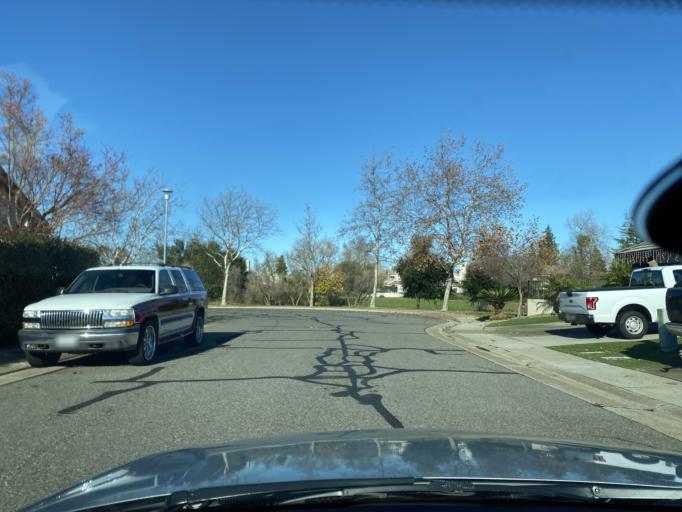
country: US
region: California
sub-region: Sacramento County
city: Elk Grove
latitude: 38.4337
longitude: -121.3815
